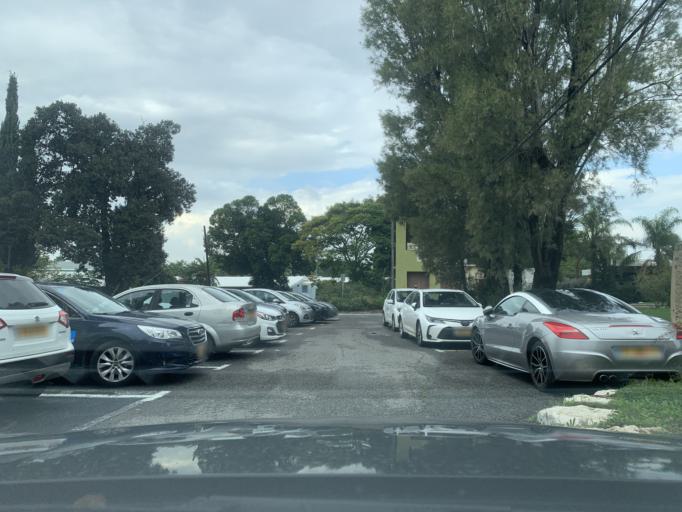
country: PS
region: West Bank
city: Qalqilyah
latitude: 32.2099
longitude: 34.9813
